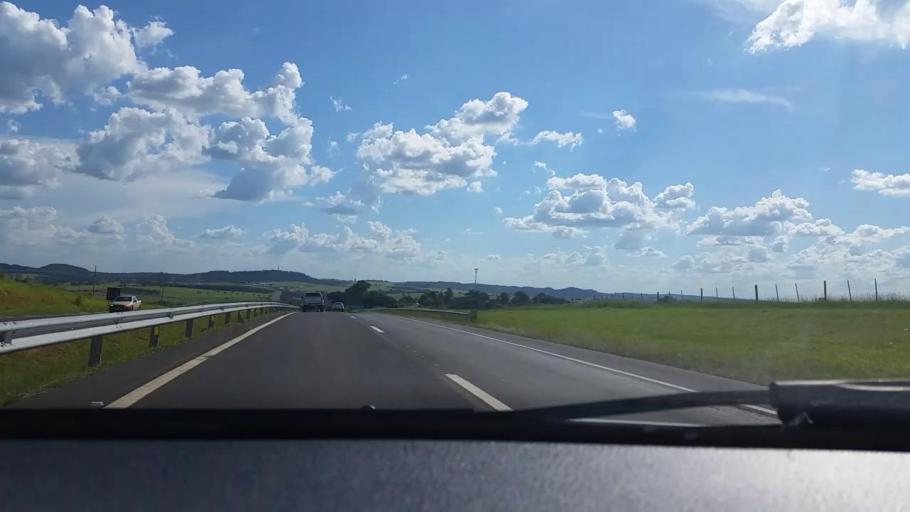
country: BR
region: Sao Paulo
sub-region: Bauru
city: Bauru
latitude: -22.3947
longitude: -49.0833
